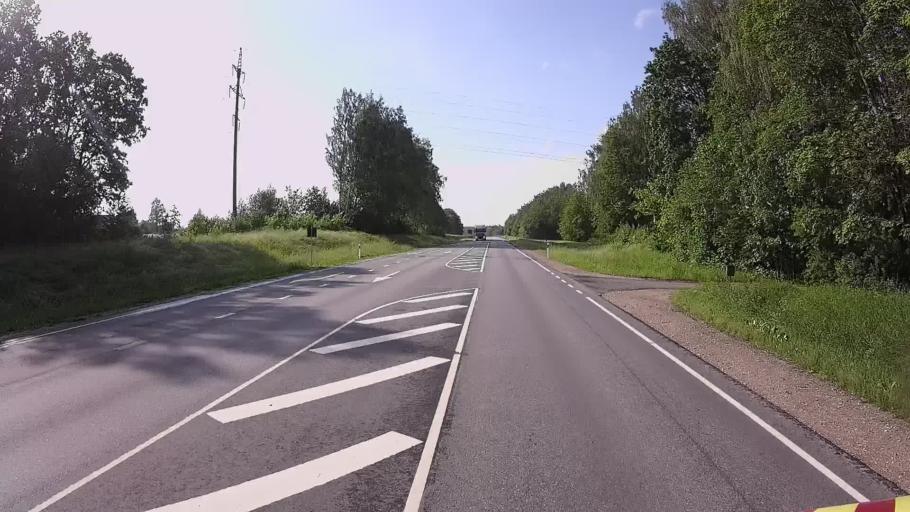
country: EE
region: Viljandimaa
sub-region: Viljandi linn
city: Viljandi
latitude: 58.3453
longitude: 25.5651
